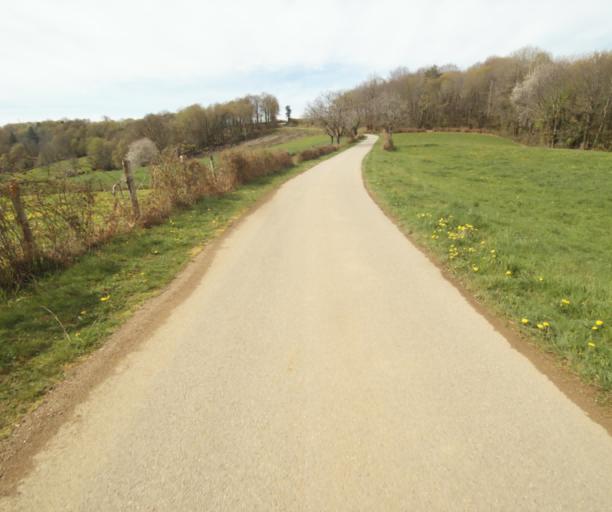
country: FR
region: Limousin
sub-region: Departement de la Correze
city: Laguenne
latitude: 45.2597
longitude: 1.8188
